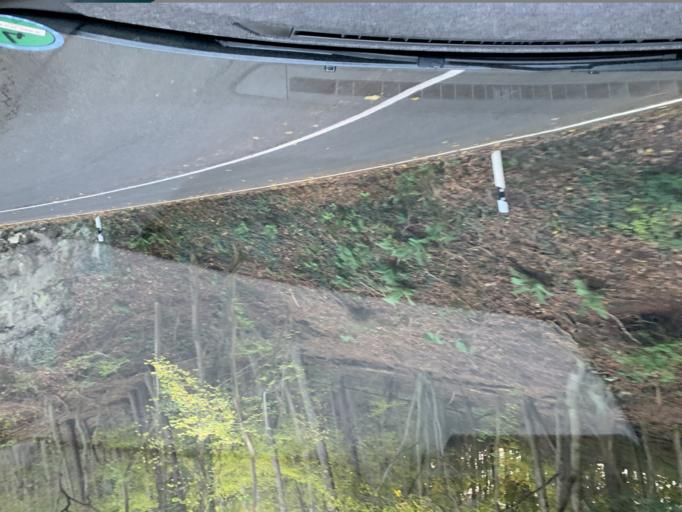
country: DE
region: North Rhine-Westphalia
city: Heimbach
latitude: 50.6273
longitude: 6.4831
